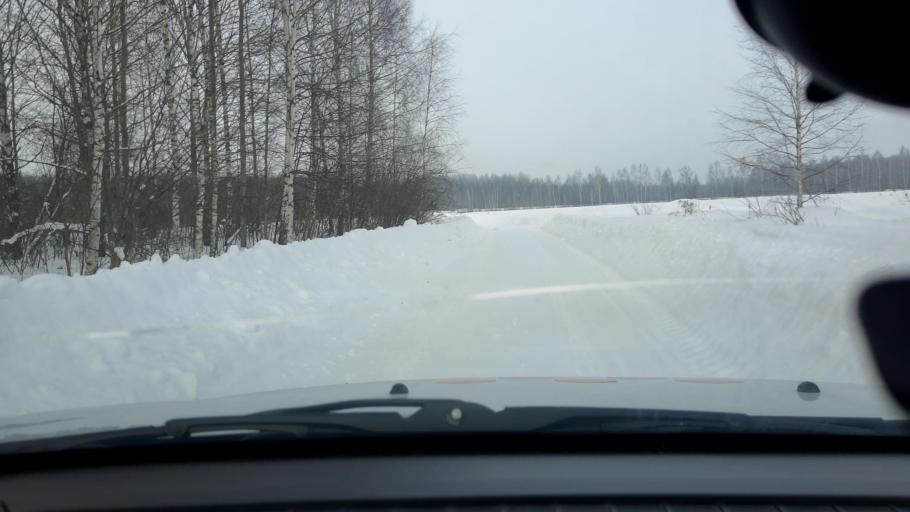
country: RU
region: Nizjnij Novgorod
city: Lukino
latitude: 56.5365
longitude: 43.7699
